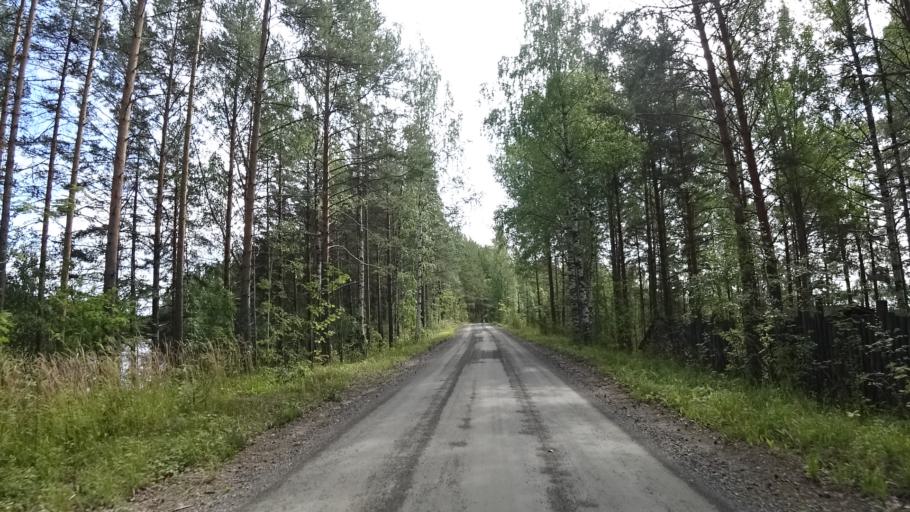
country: FI
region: North Karelia
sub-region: Joensuu
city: Pyhaeselkae
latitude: 62.3784
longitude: 29.8100
